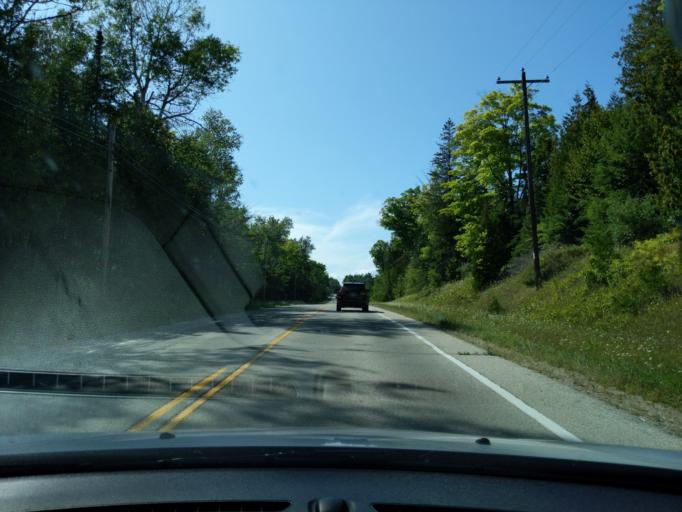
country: US
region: Michigan
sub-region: Delta County
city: Escanaba
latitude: 45.2592
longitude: -87.0587
